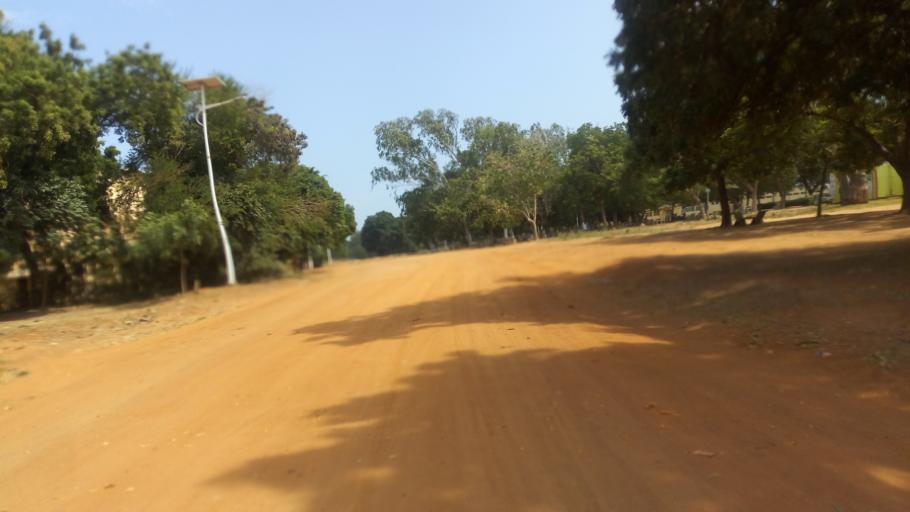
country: TG
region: Maritime
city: Lome
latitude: 6.1761
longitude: 1.2147
